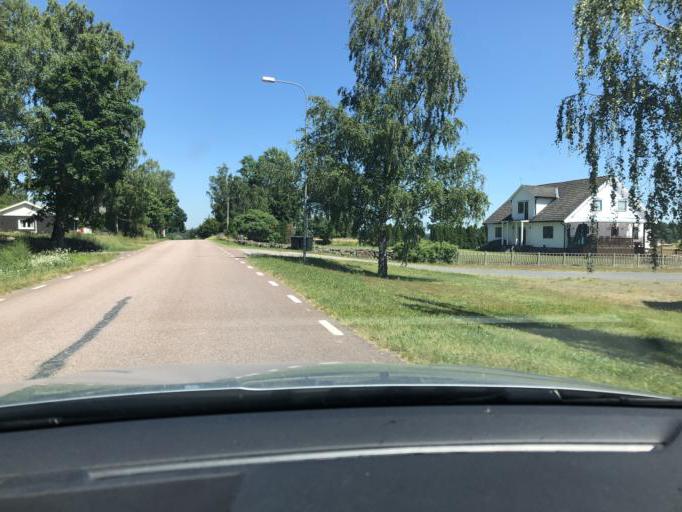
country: SE
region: Blekinge
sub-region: Olofstroms Kommun
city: Jamshog
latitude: 56.1705
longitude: 14.6052
